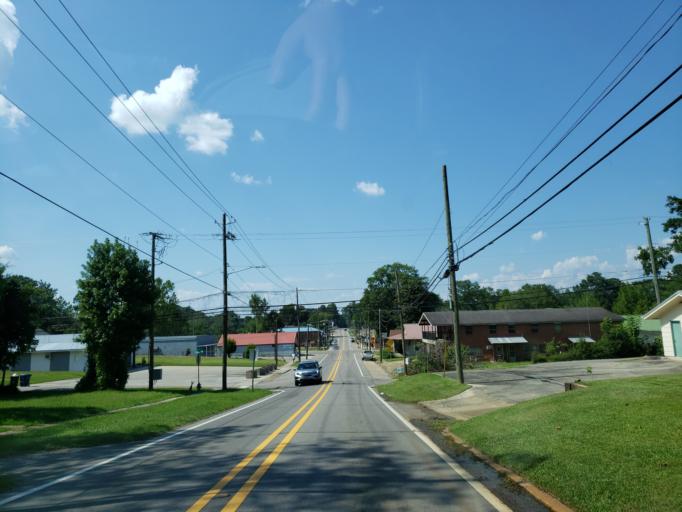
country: US
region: Mississippi
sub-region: Lamar County
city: Sumrall
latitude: 31.4142
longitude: -89.5458
